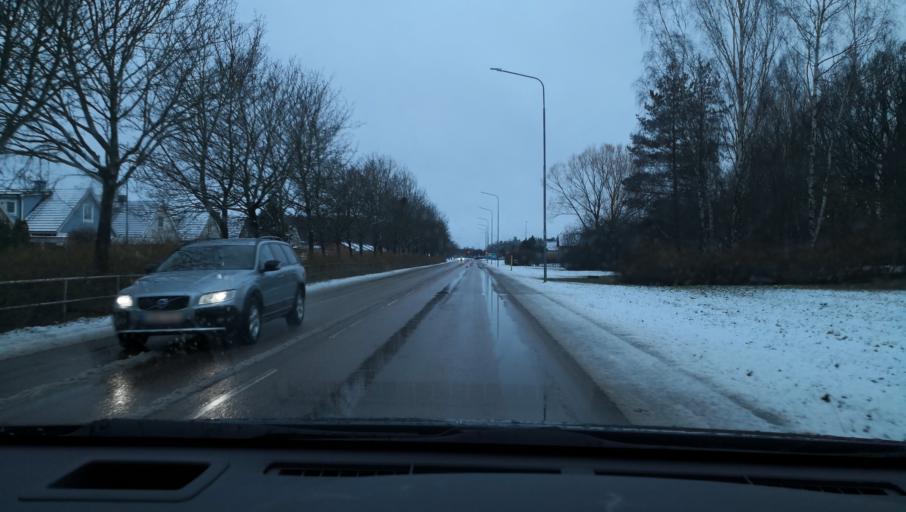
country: SE
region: Vaestmanland
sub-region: Kopings Kommun
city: Koping
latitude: 59.5180
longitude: 16.0096
